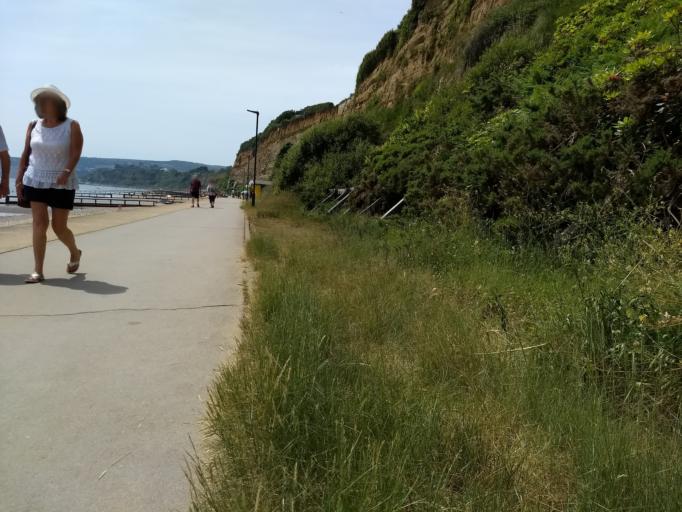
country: GB
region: England
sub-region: Isle of Wight
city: Sandown
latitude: 50.6485
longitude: -1.1616
